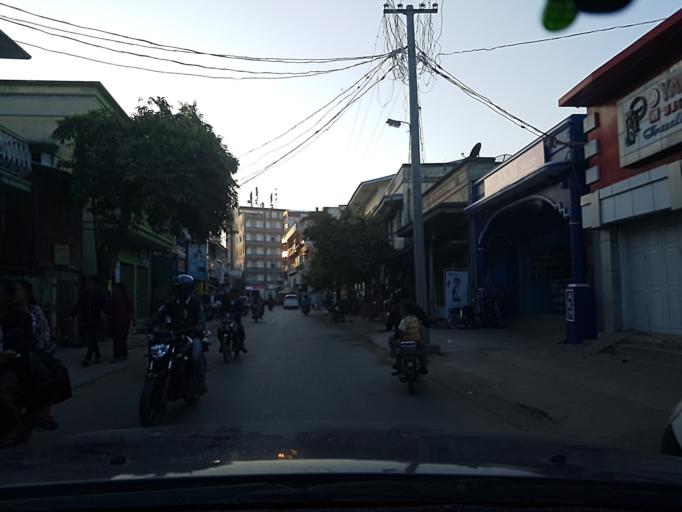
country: MM
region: Sagain
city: Monywa
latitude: 22.1122
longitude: 95.1340
